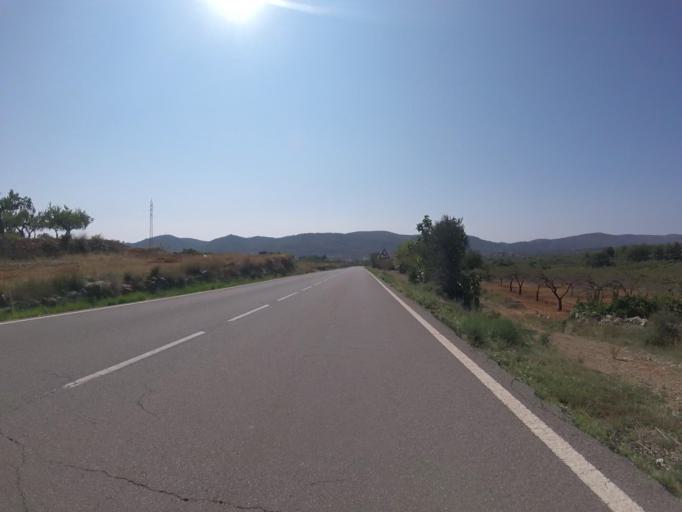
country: ES
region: Valencia
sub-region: Provincia de Castello
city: Adzaneta
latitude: 40.2292
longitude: -0.1755
